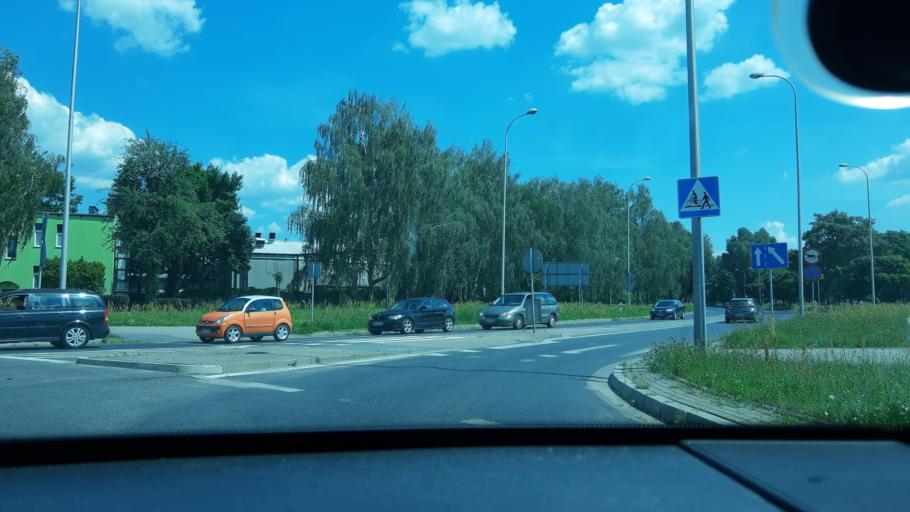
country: PL
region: Lodz Voivodeship
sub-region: Powiat zdunskowolski
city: Zdunska Wola
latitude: 51.6063
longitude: 18.9389
